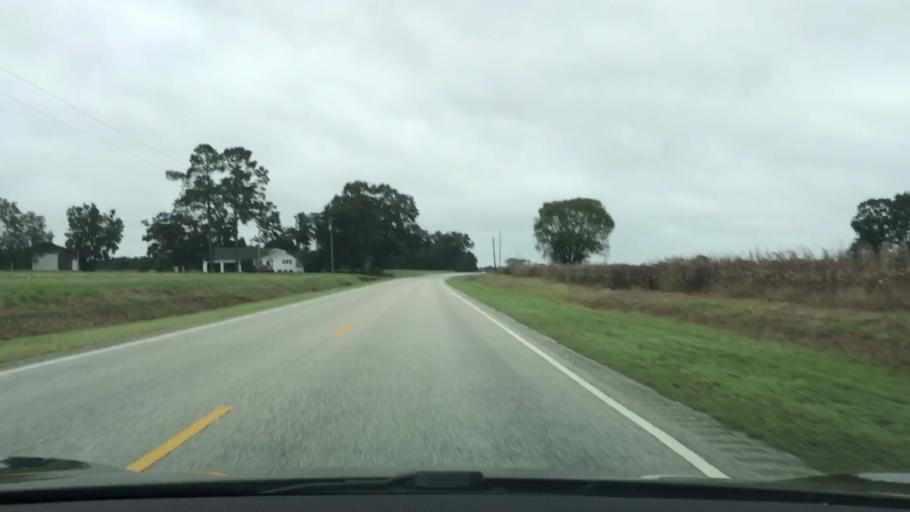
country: US
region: Alabama
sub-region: Coffee County
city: Elba
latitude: 31.3298
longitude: -86.1331
